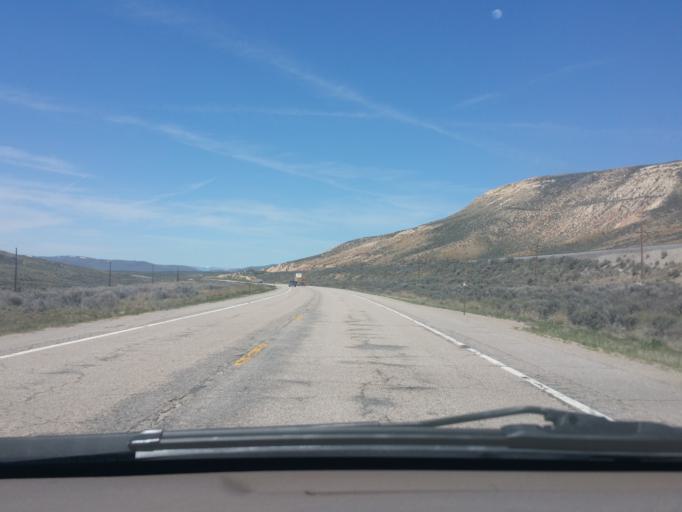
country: US
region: Wyoming
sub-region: Lincoln County
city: Kemmerer
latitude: 41.8157
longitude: -110.6327
